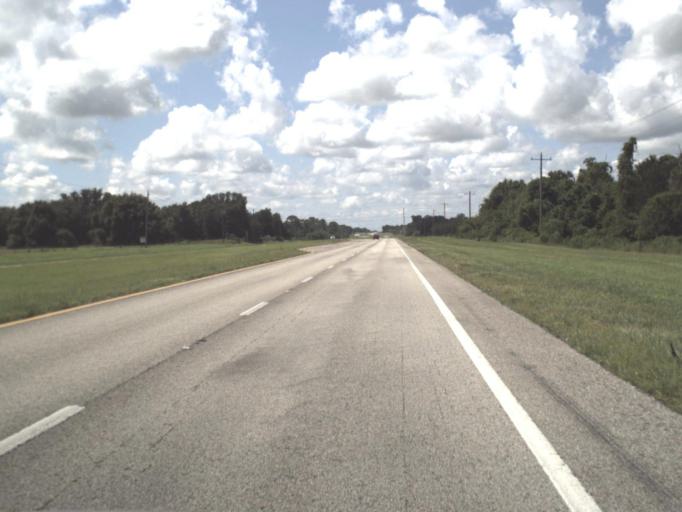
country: US
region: Florida
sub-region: DeSoto County
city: Arcadia
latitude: 27.3247
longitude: -81.8127
